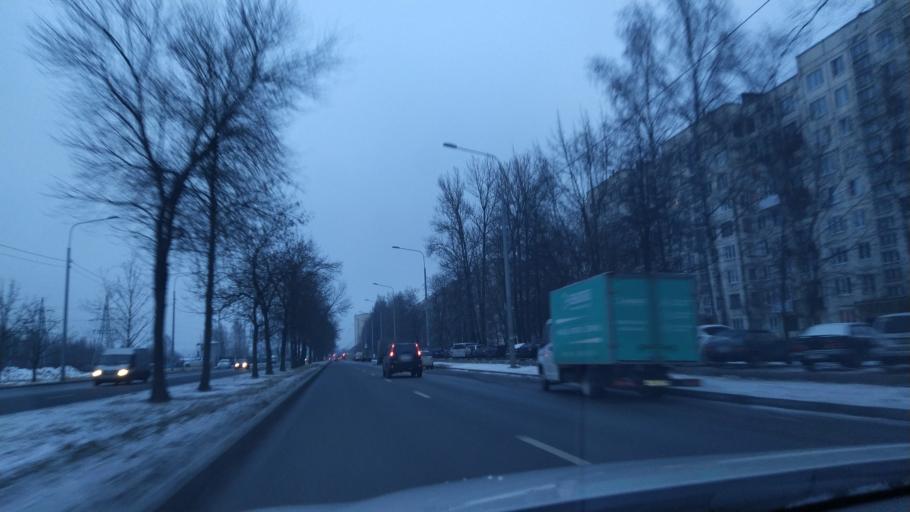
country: RU
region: St.-Petersburg
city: Grazhdanka
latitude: 60.0180
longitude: 30.4218
